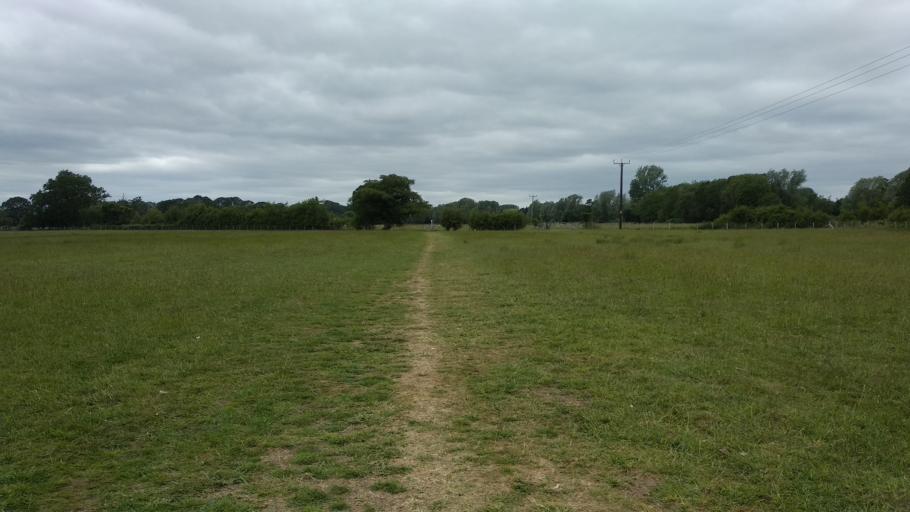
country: GB
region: England
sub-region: Kent
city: Ashford
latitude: 51.1547
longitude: 0.8303
